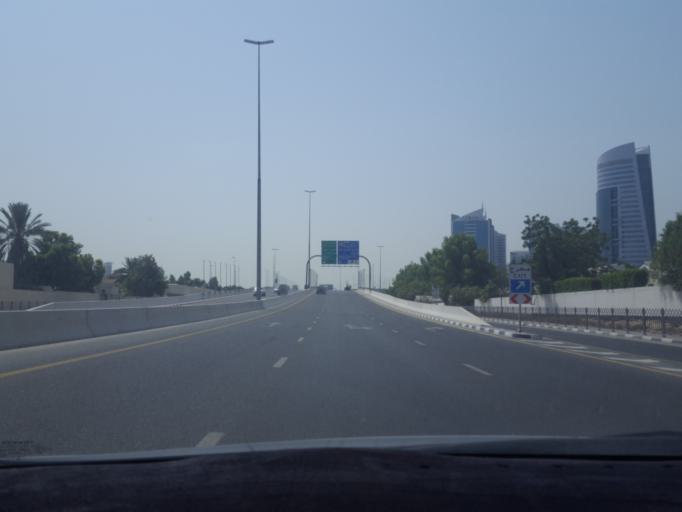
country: AE
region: Dubai
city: Dubai
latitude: 25.1074
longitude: 55.1743
